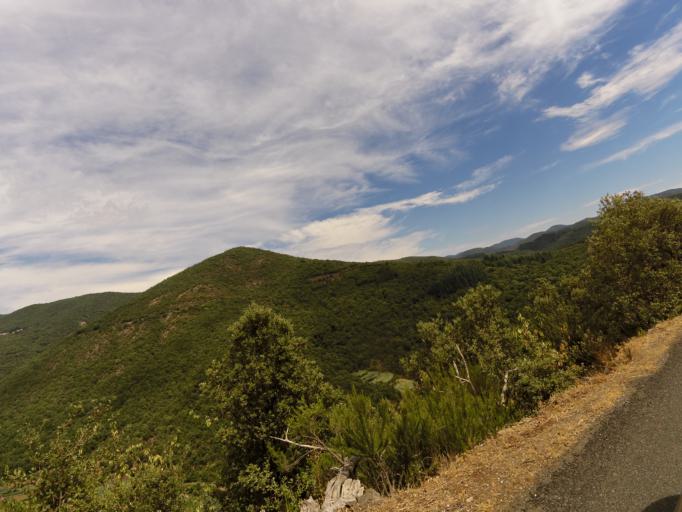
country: FR
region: Languedoc-Roussillon
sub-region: Departement du Gard
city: Le Vigan
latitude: 44.0162
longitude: 3.6421
